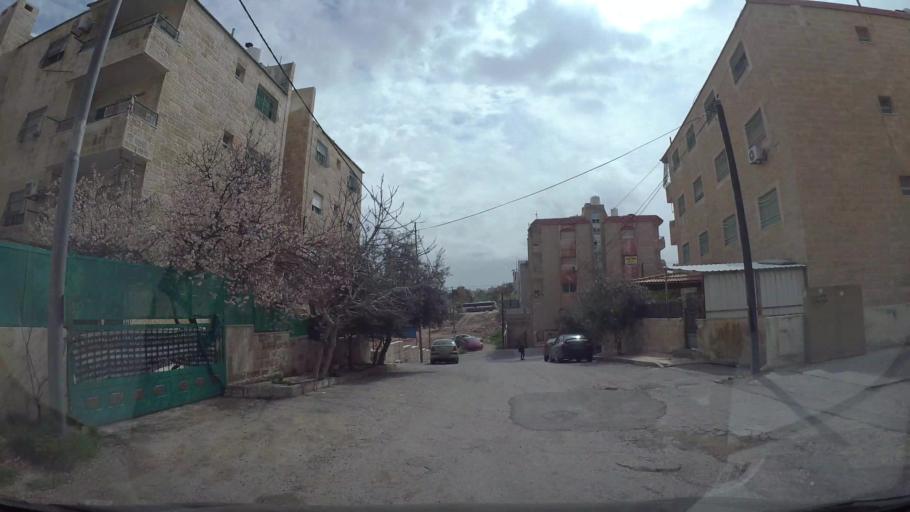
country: JO
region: Amman
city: Amman
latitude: 31.9915
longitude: 35.9421
